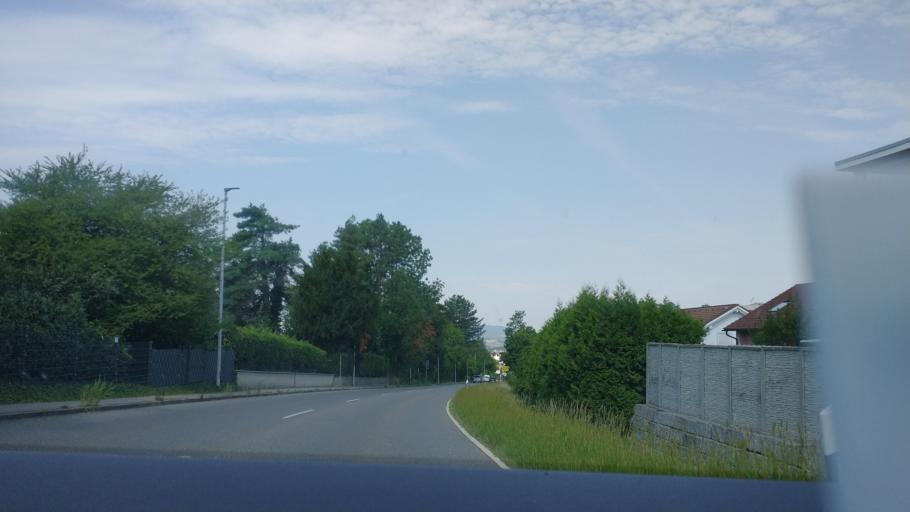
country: DE
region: Baden-Wuerttemberg
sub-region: Tuebingen Region
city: Tettnang
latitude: 47.6698
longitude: 9.6006
